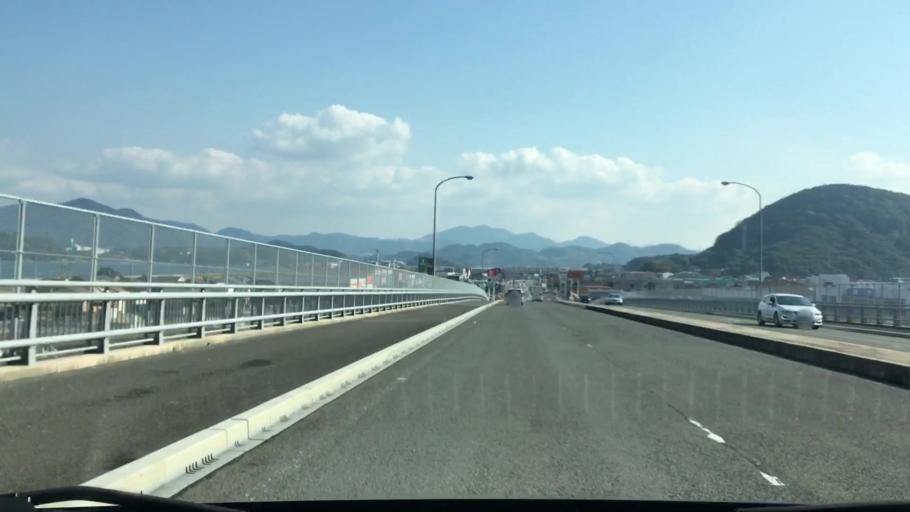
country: JP
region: Nagasaki
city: Togitsu
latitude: 32.8544
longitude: 129.8227
